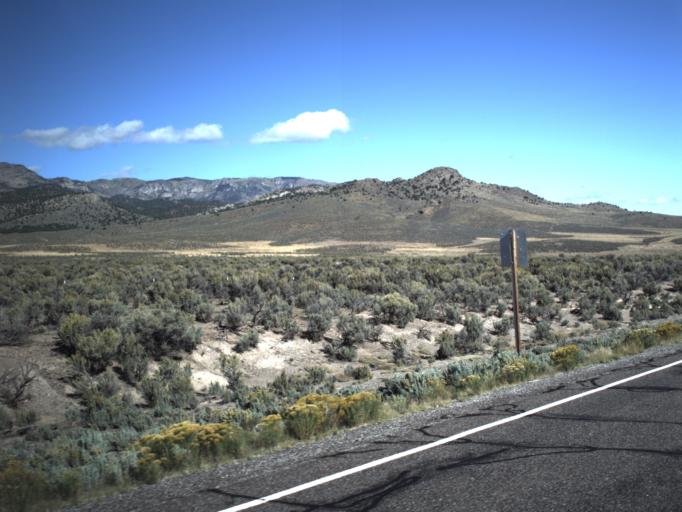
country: US
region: Utah
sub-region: Piute County
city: Junction
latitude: 38.2892
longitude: -111.9774
